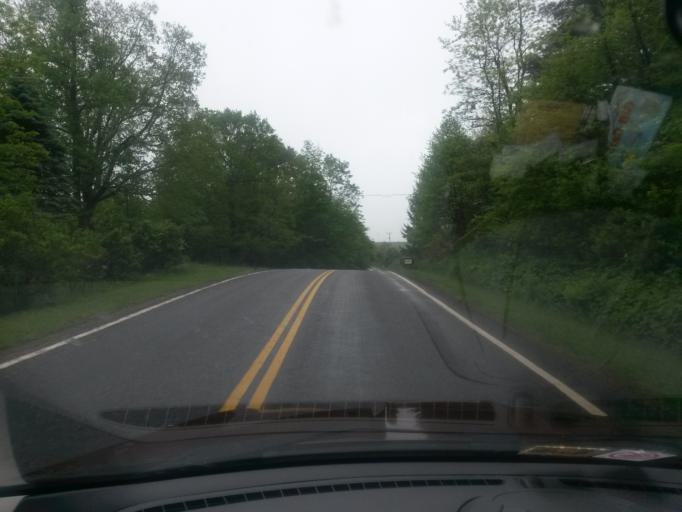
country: US
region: Virginia
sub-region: Floyd County
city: Floyd
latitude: 36.7677
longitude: -80.3881
